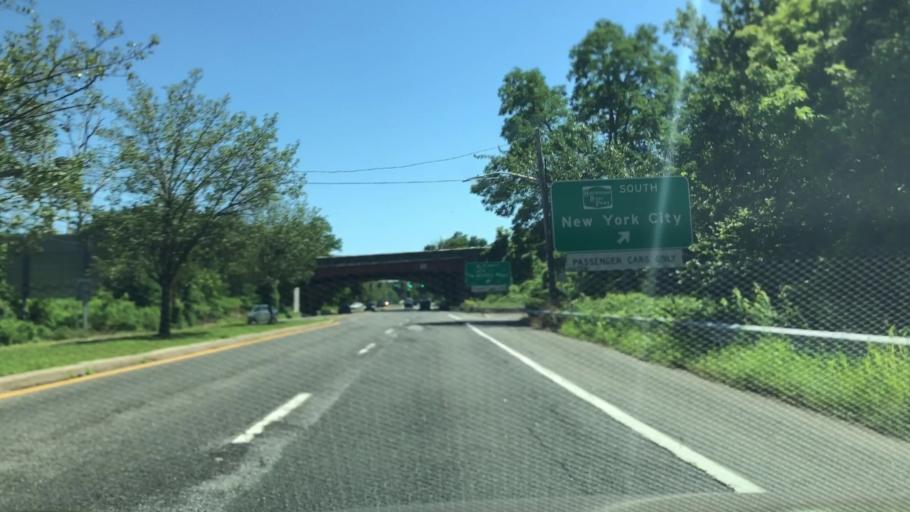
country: US
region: New York
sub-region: Westchester County
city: Harrison
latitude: 40.9846
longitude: -73.7445
